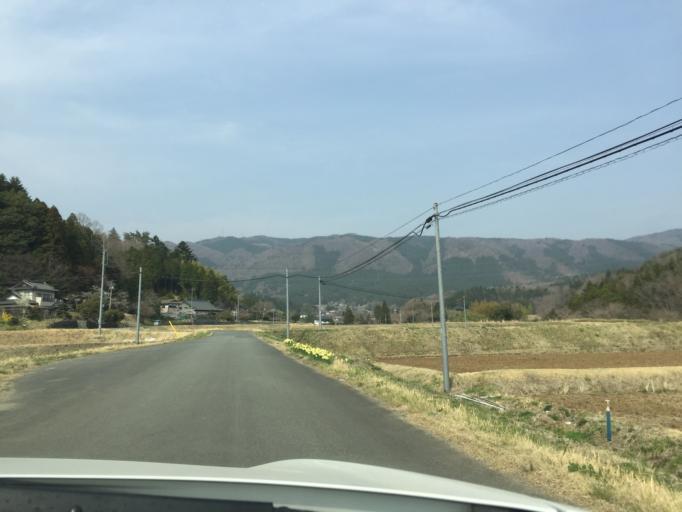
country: JP
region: Fukushima
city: Iwaki
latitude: 37.0253
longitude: 140.7326
